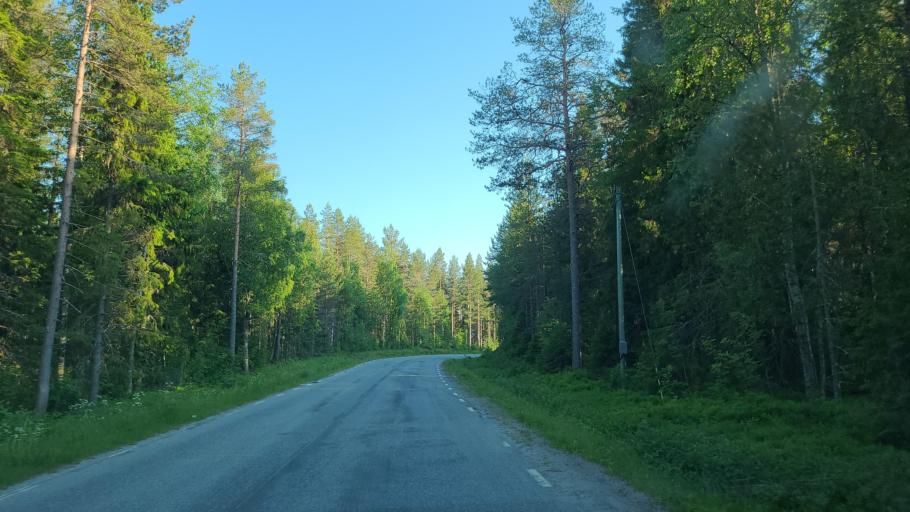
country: SE
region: Vaesterbotten
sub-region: Skelleftea Kommun
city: Burea
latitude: 64.3558
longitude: 21.3380
